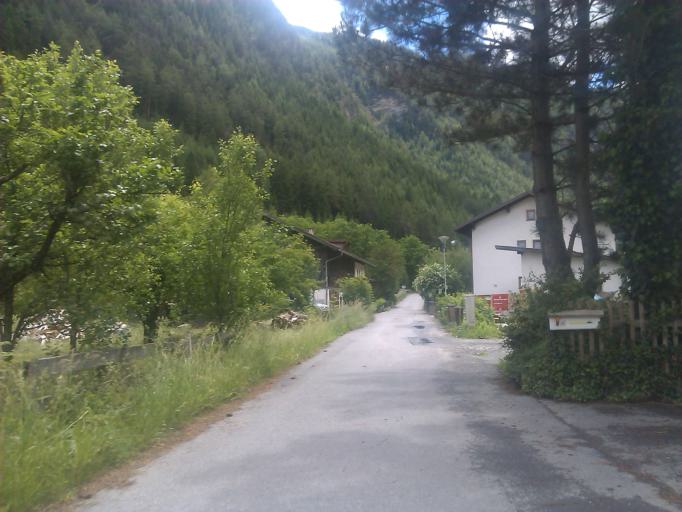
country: AT
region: Tyrol
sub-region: Politischer Bezirk Landeck
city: Fiss
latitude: 47.0296
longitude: 10.6267
